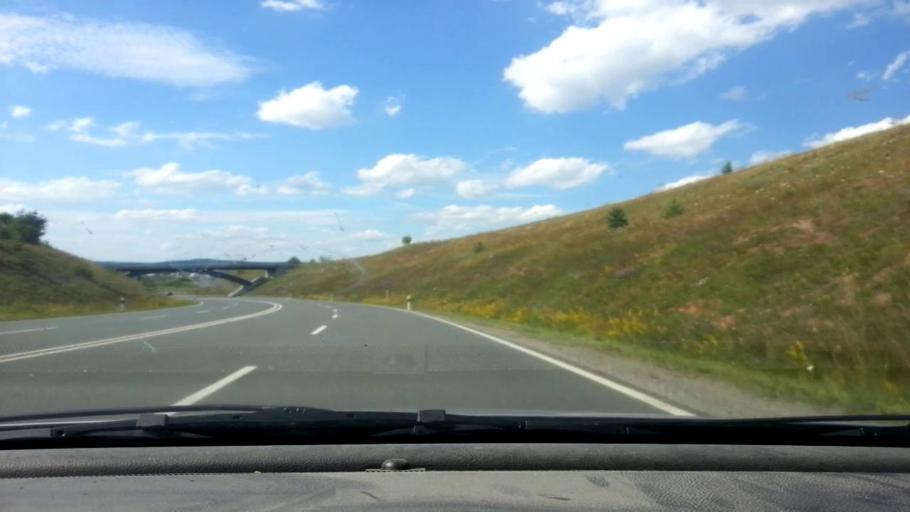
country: DE
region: Bavaria
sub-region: Upper Franconia
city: Bayreuth
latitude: 49.9257
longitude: 11.6050
